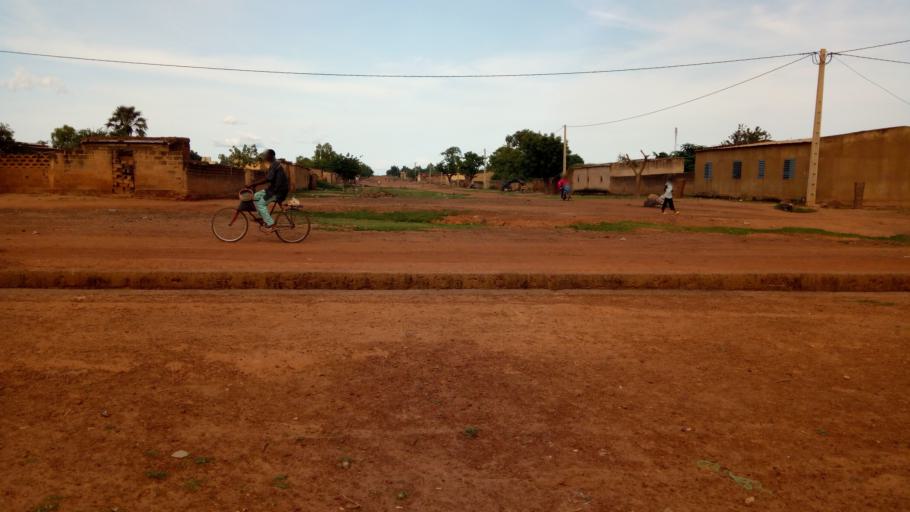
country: ML
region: Sikasso
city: Koutiala
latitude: 12.4105
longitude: -5.4648
